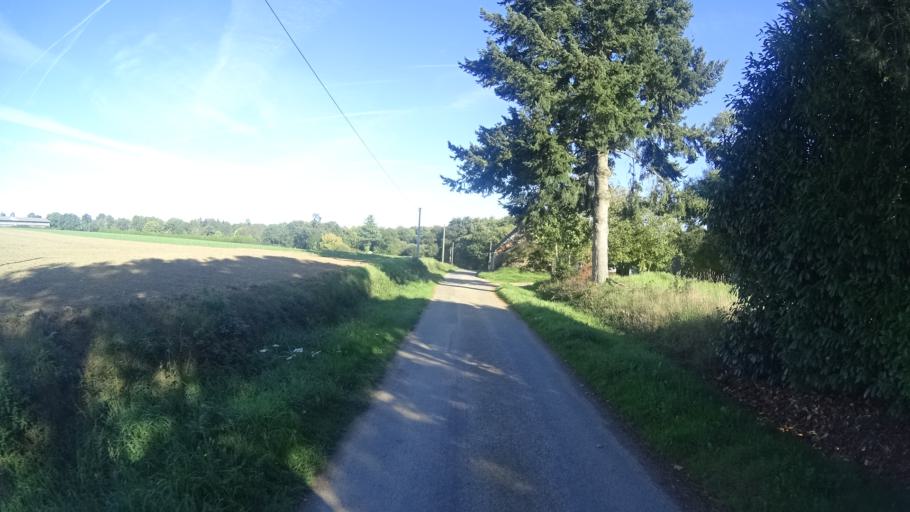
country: FR
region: Brittany
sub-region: Departement du Morbihan
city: Saint-Vincent-sur-Oust
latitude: 47.7040
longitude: -2.1754
